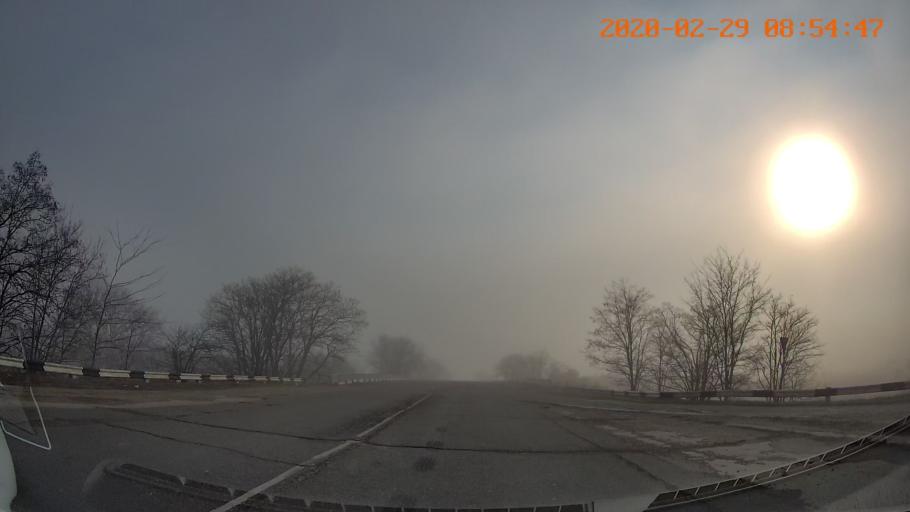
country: MD
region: Telenesti
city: Tiraspolul Nou
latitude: 46.9277
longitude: 29.5810
